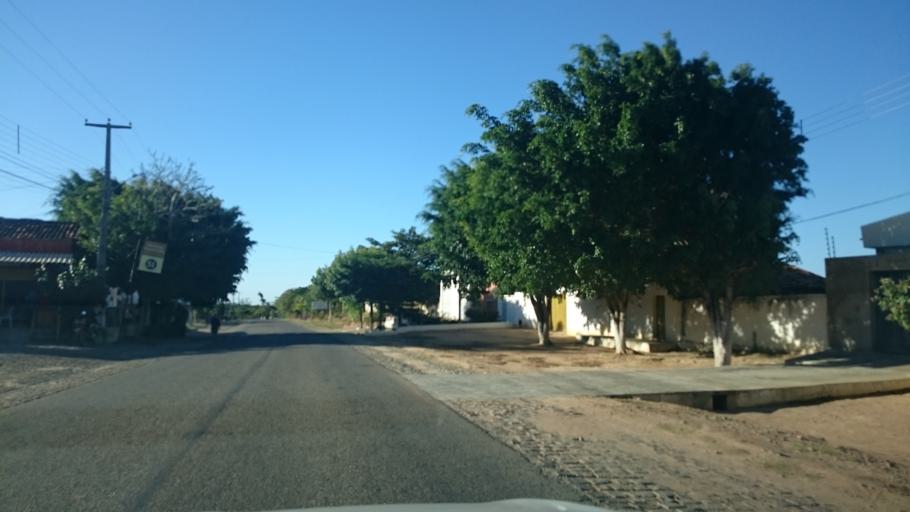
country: BR
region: Rio Grande do Norte
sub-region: Umarizal
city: Umarizal
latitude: -6.0719
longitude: -37.9331
